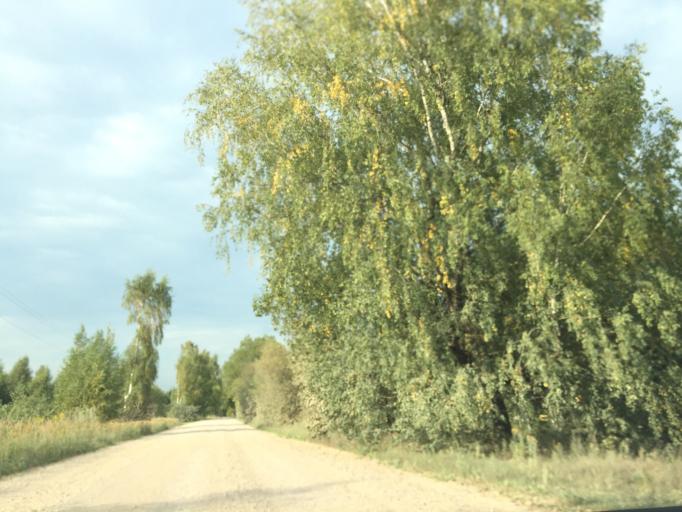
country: LV
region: Ikskile
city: Ikskile
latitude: 56.8167
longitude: 24.4488
